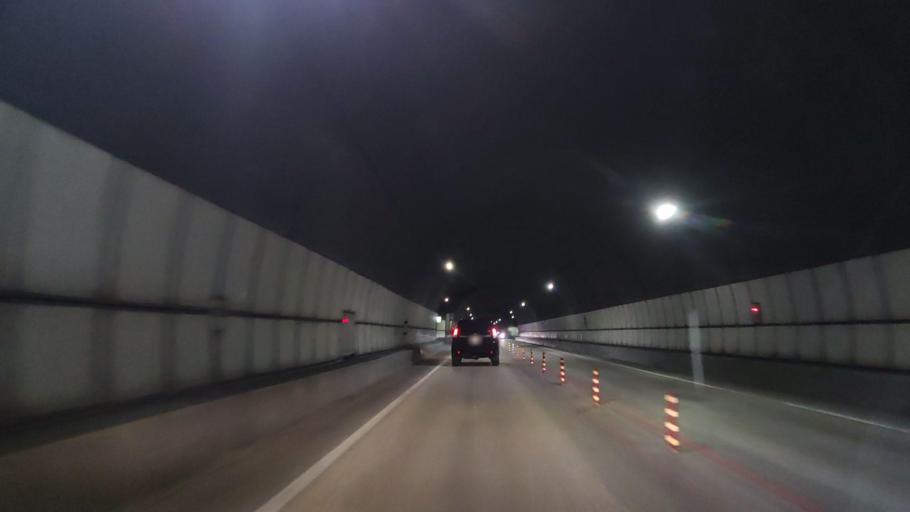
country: JP
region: Yamagata
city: Shinjo
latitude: 38.6849
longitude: 140.3155
